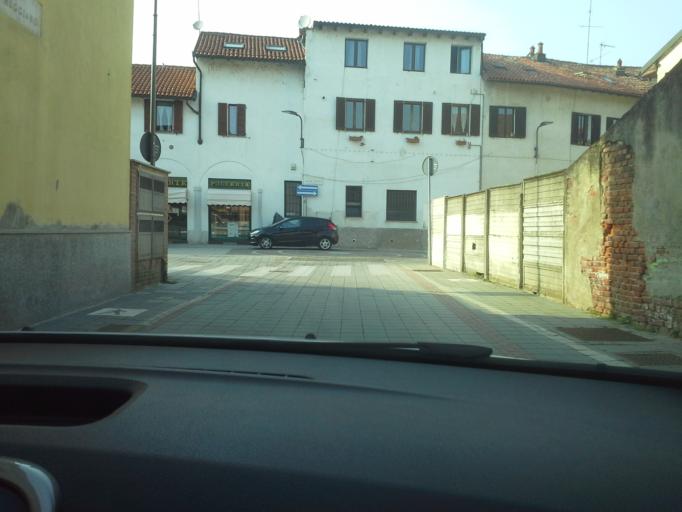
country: IT
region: Lombardy
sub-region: Citta metropolitana di Milano
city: Cesano Boscone
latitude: 45.4492
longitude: 9.0686
